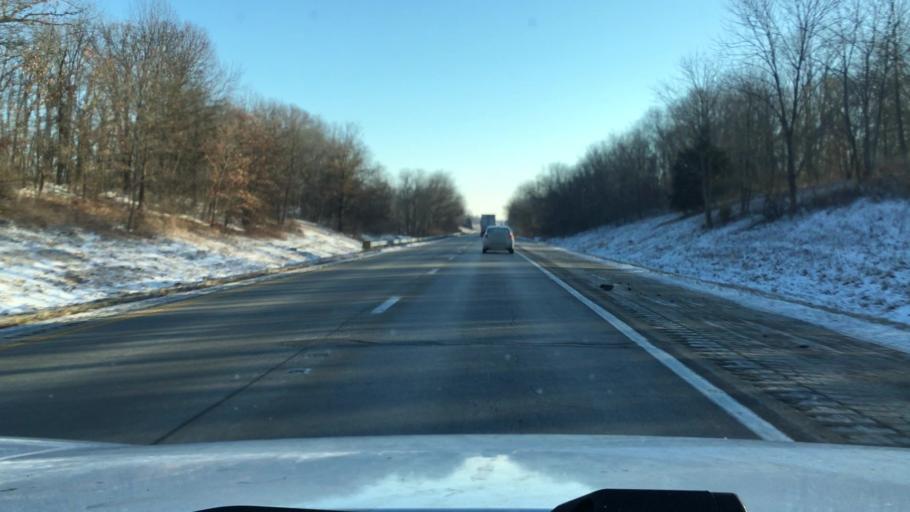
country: US
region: Illinois
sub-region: Effingham County
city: Effingham
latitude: 39.0789
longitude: -88.6339
